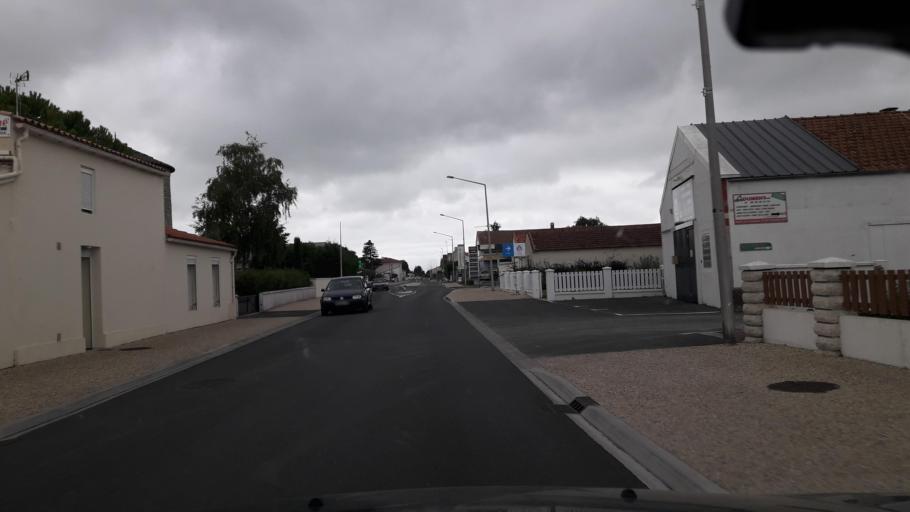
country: FR
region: Poitou-Charentes
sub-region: Departement de la Charente-Maritime
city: Arvert
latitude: 45.7418
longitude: -1.1206
